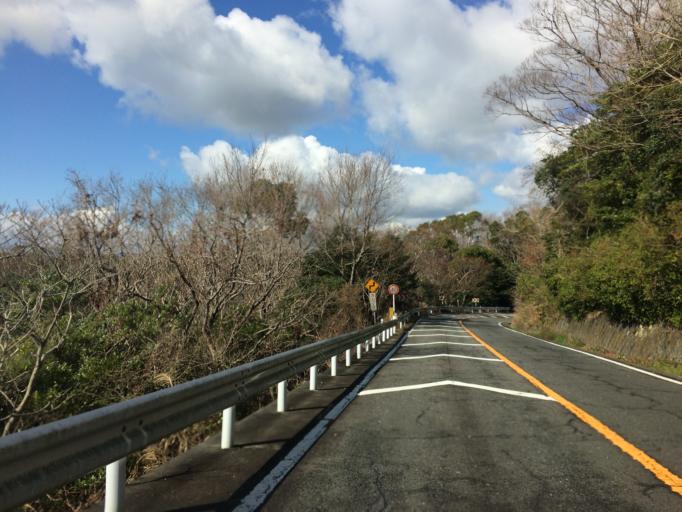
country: JP
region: Shizuoka
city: Shizuoka-shi
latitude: 34.9722
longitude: 138.4594
